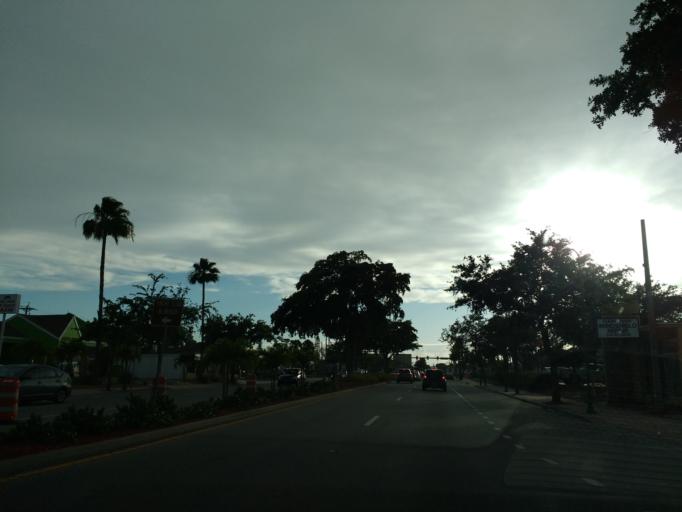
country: US
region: Florida
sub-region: Lee County
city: Cape Coral
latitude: 26.5628
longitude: -81.9562
